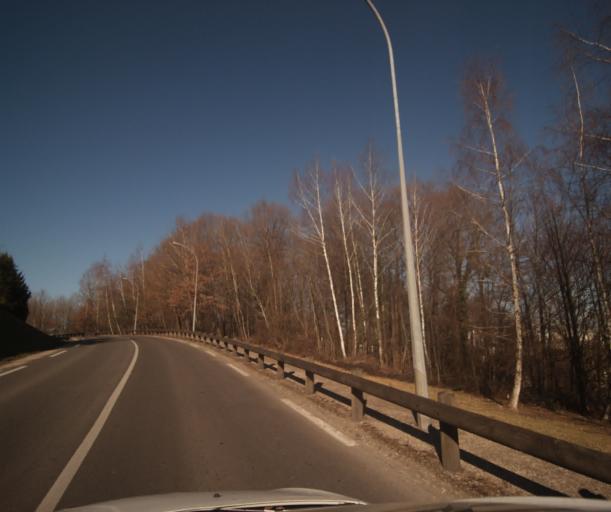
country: FR
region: Franche-Comte
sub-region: Departement du Doubs
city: Avanne-Aveney
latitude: 47.2169
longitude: 5.9591
